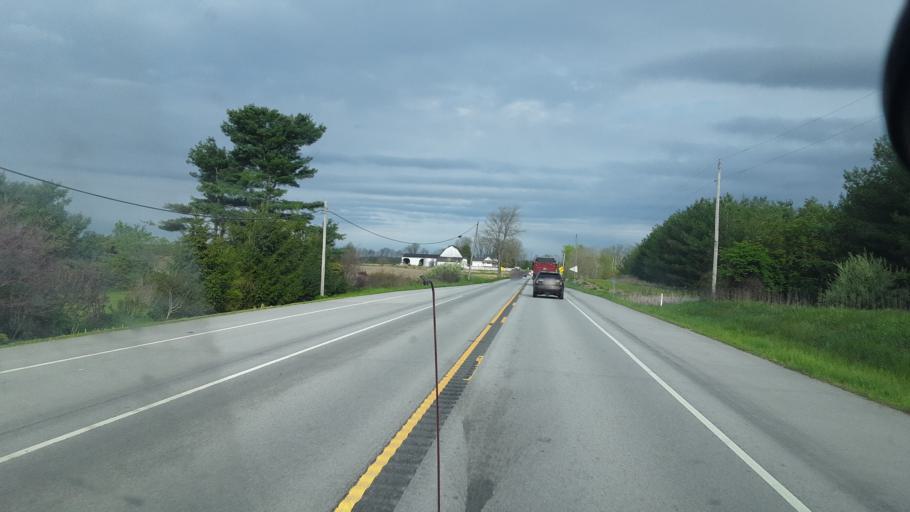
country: US
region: Indiana
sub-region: Whitley County
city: Tri-Lakes
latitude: 41.2625
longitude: -85.3868
